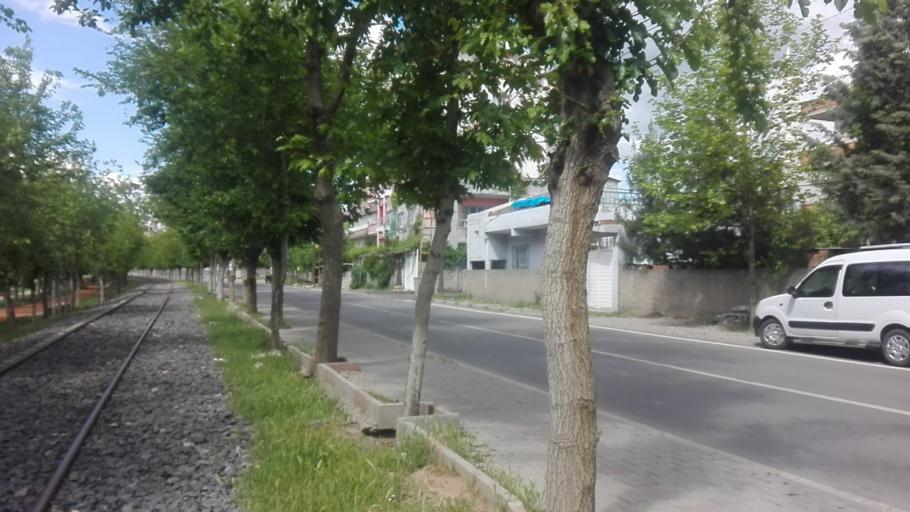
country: TR
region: Batman
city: Batman
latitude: 37.8939
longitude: 41.1460
